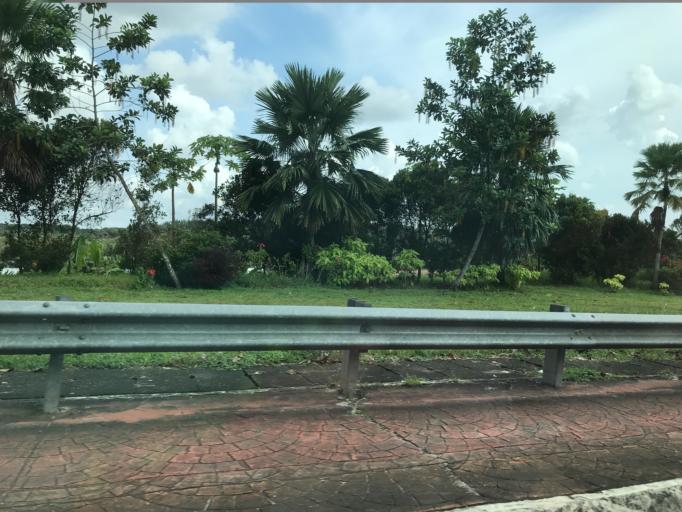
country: MY
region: Johor
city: Taman Senai
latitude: 1.6047
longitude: 103.6478
